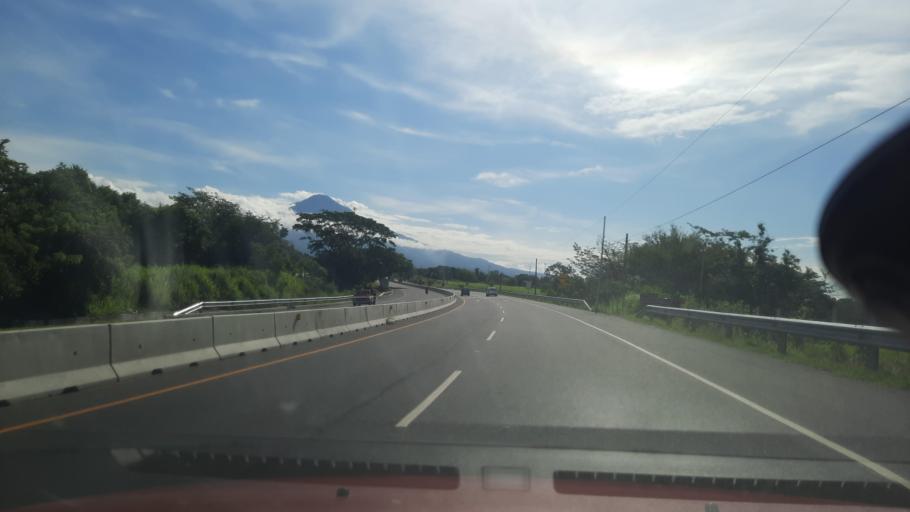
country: SV
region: La Paz
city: Santiago Nonualco
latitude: 13.4872
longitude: -88.9569
